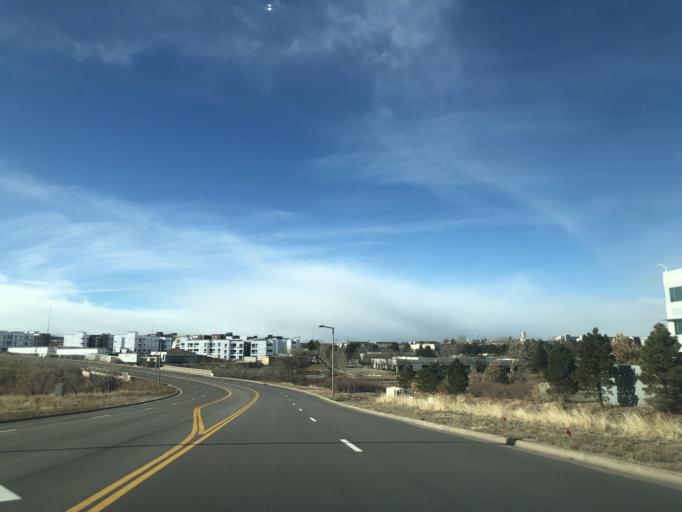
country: US
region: Colorado
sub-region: Douglas County
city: Meridian
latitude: 39.5581
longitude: -104.8598
